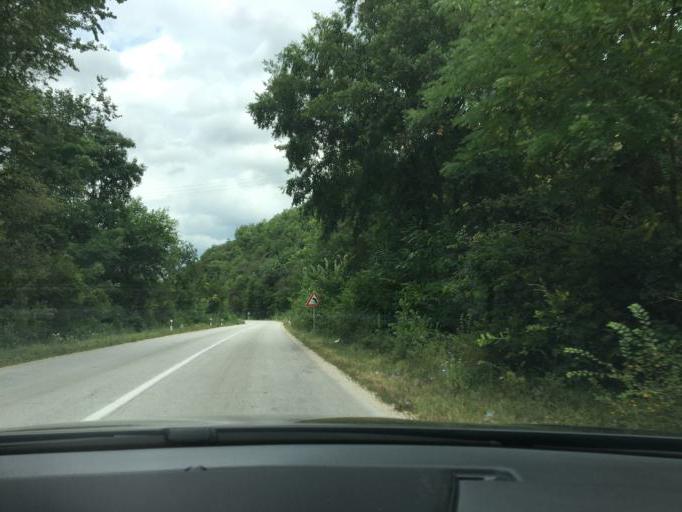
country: MK
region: Kriva Palanka
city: Kriva Palanka
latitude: 42.1733
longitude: 22.2329
